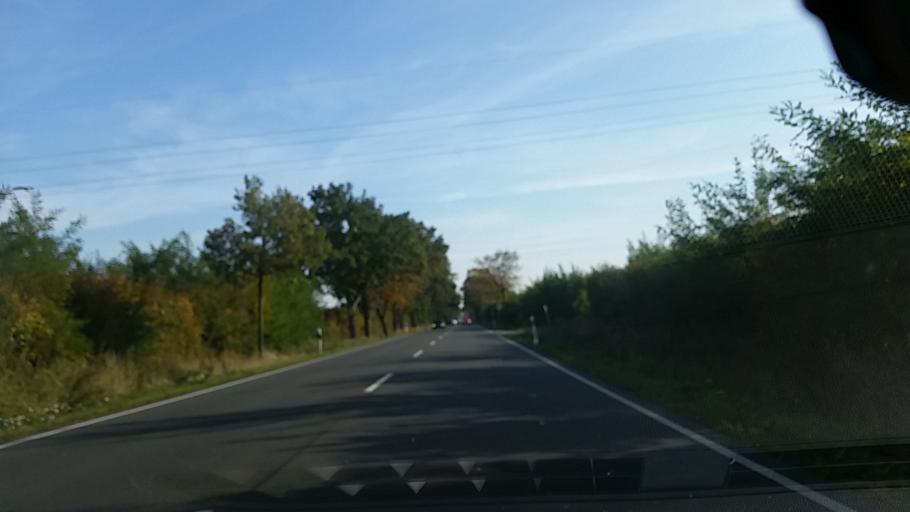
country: DE
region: Lower Saxony
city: Didderse
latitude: 52.3566
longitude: 10.3994
